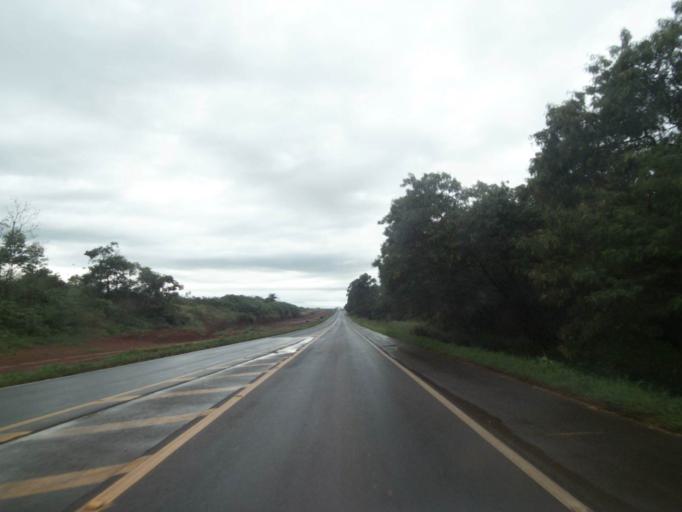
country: BR
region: Parana
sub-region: Toledo
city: Toledo
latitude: -24.6900
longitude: -53.7620
